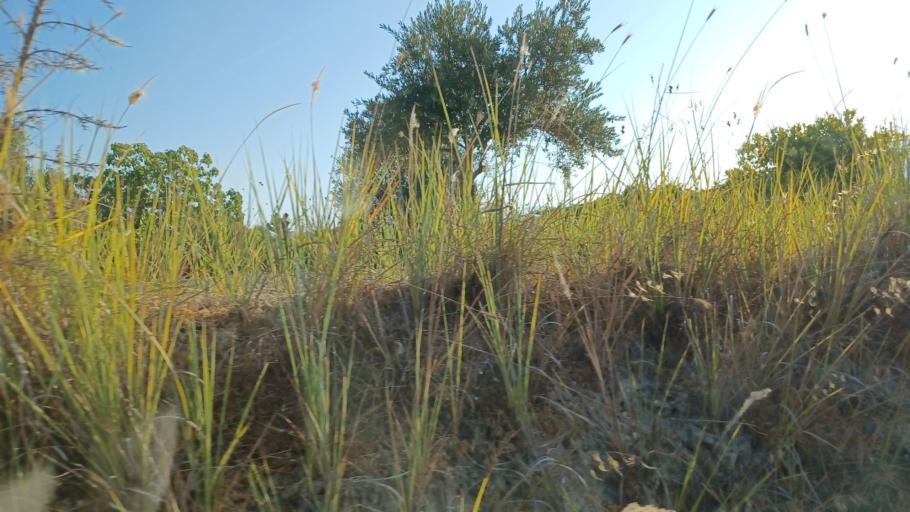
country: CY
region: Pafos
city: Mesogi
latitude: 34.8738
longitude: 32.5090
